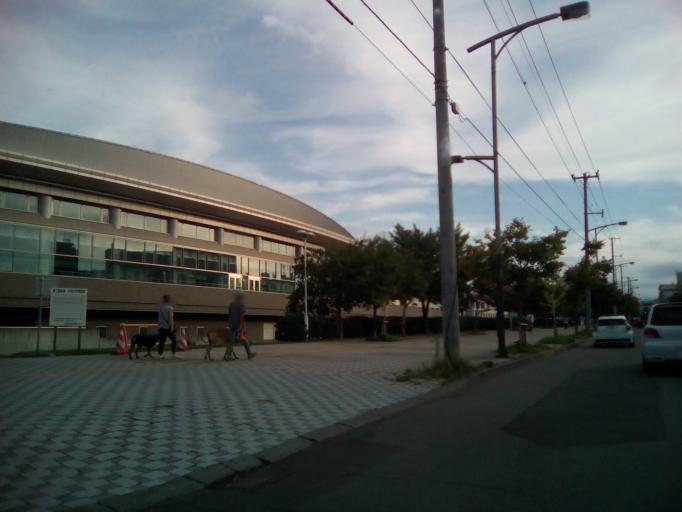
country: JP
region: Hokkaido
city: Sapporo
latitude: 43.0456
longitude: 141.3768
